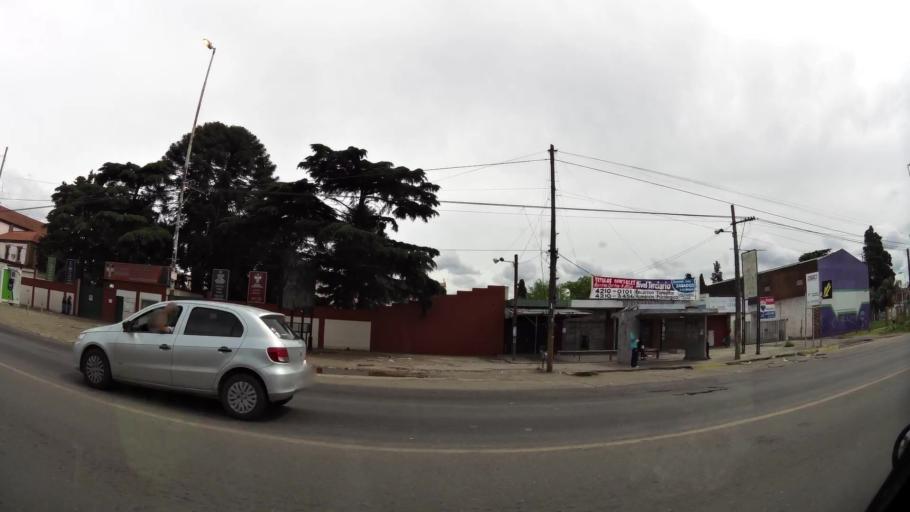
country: AR
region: Buenos Aires
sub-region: Partido de Quilmes
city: Quilmes
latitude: -34.7685
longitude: -58.2722
